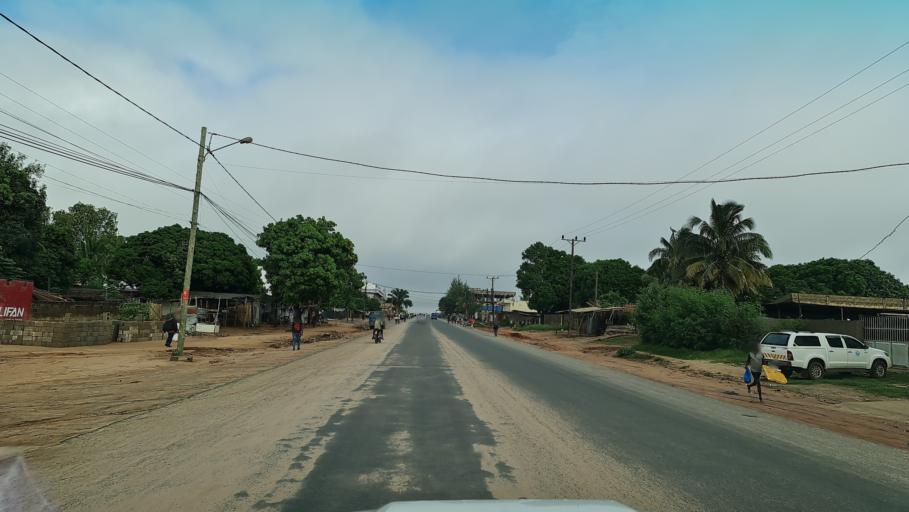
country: MZ
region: Nampula
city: Nampula
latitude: -15.1381
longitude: 39.2849
